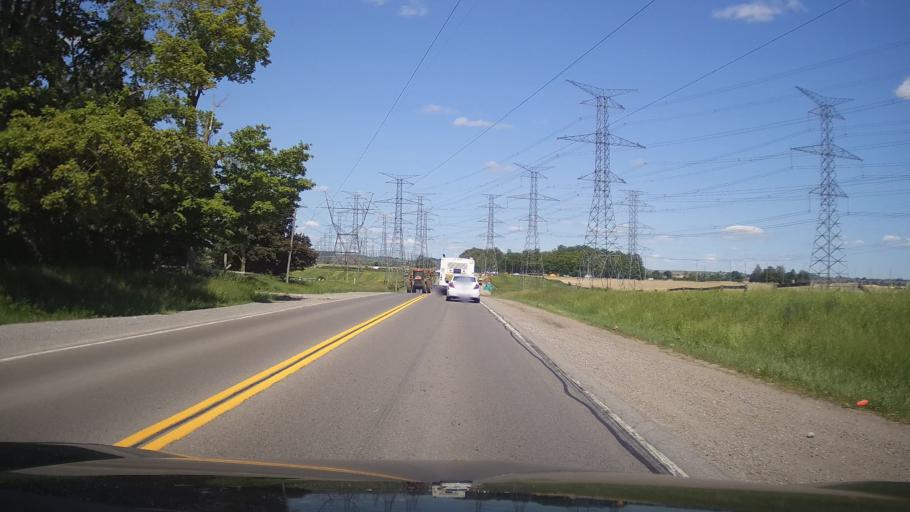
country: CA
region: Ontario
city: Oshawa
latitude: 43.9648
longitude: -78.9118
